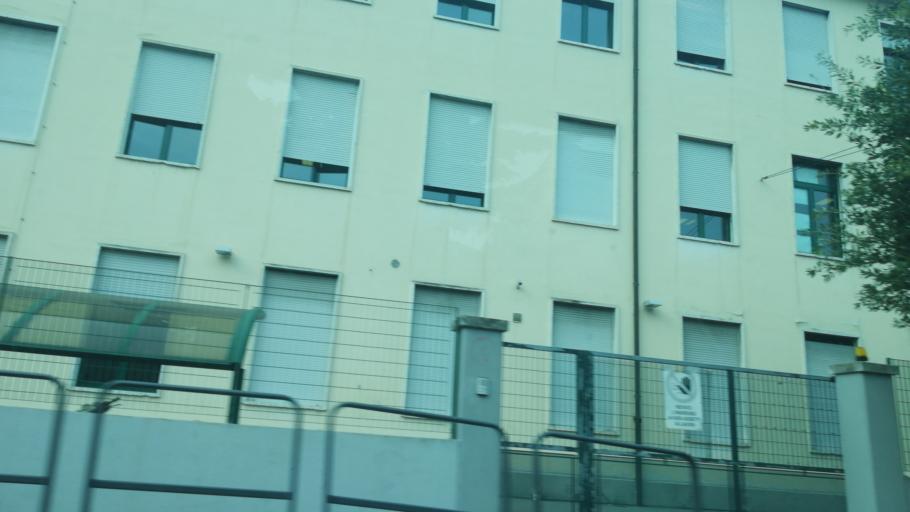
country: IT
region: Veneto
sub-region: Provincia di Venezia
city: Mestre
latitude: 45.4962
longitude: 12.2484
